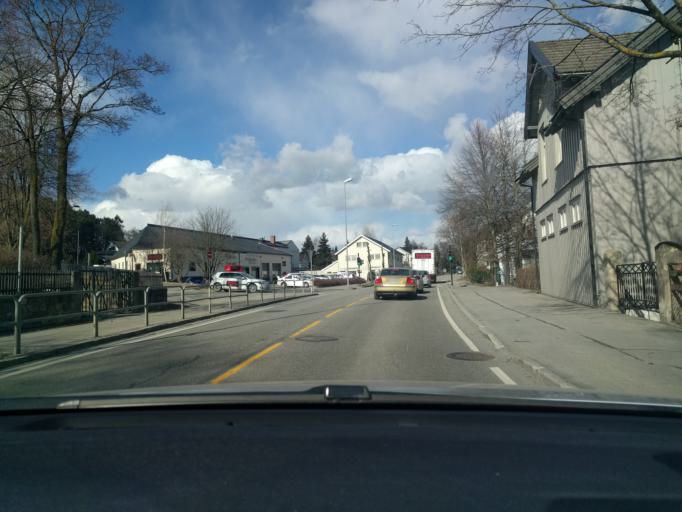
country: NO
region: Hedmark
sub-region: Hamar
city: Hamar
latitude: 60.7996
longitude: 11.0724
